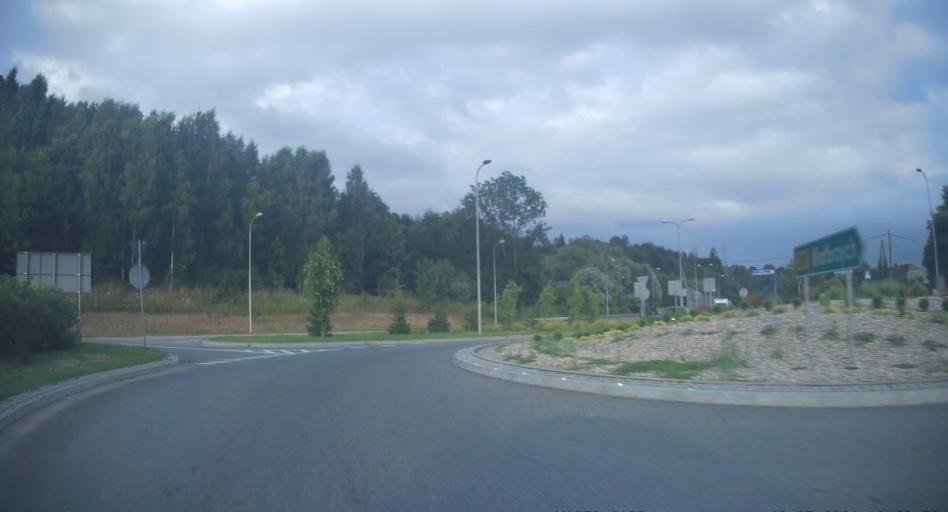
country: PL
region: Lower Silesian Voivodeship
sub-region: Powiat klodzki
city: Ludwikowice Klodzkie
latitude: 50.6151
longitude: 16.4870
